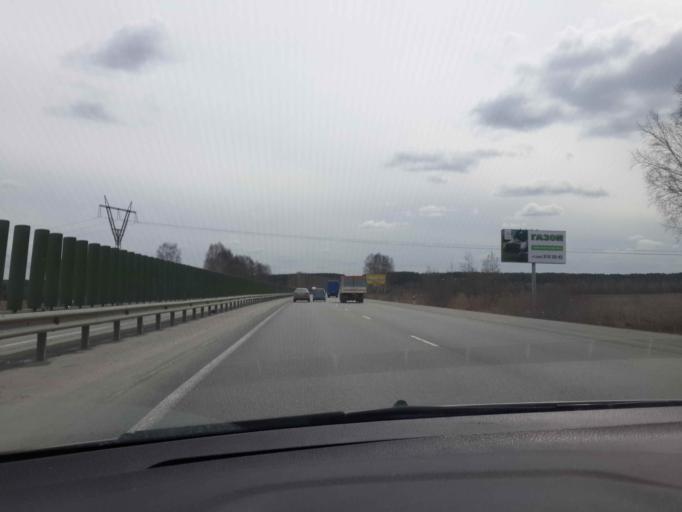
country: RU
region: Sverdlovsk
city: Istok
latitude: 56.7928
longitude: 60.8253
